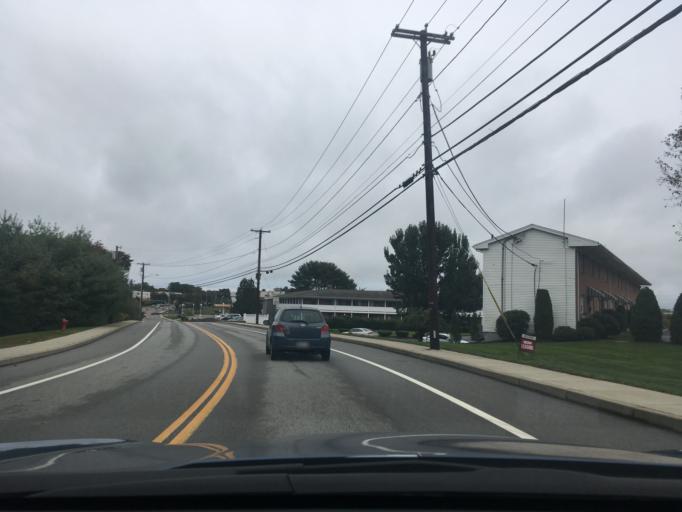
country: US
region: Rhode Island
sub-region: Kent County
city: East Greenwich
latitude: 41.6061
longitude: -71.4591
